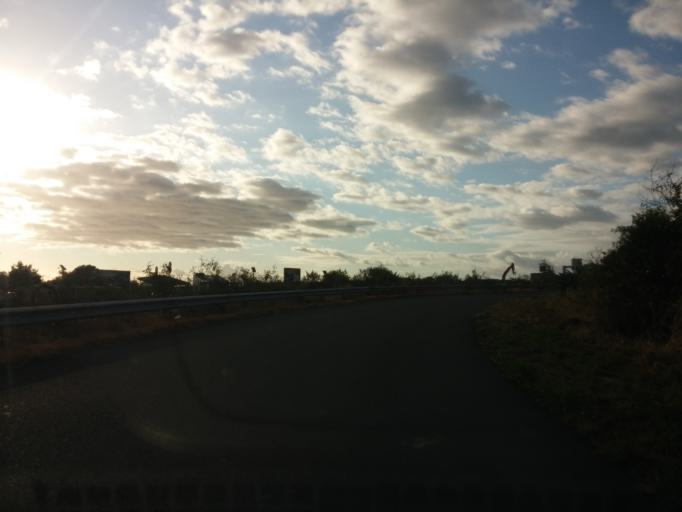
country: RE
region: Reunion
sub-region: Reunion
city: Le Port
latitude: -20.9701
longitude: 55.2993
